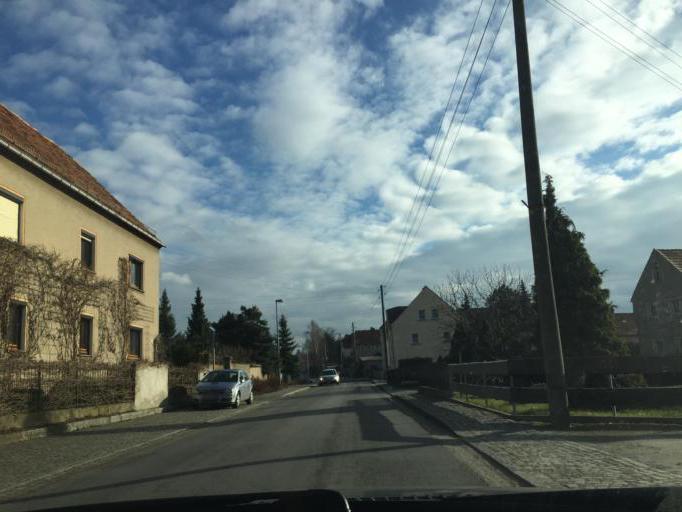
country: DE
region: Saxony
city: Ebersbach
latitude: 51.2326
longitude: 13.6584
